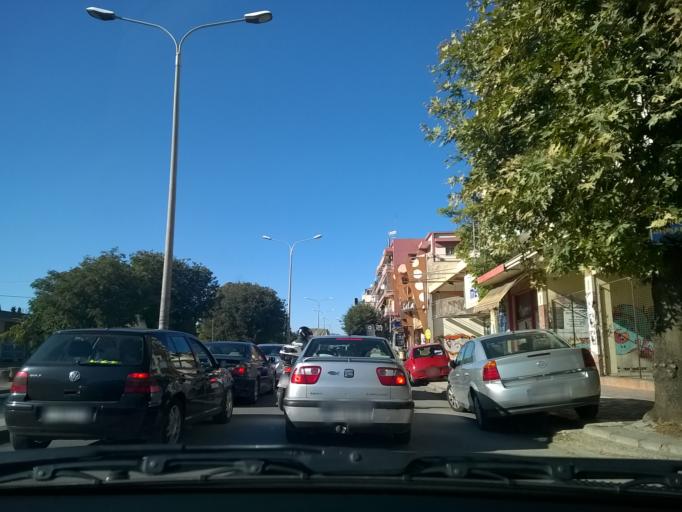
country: GR
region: Central Macedonia
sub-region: Nomos Thessalonikis
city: Ampelokipoi
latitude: 40.6527
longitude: 22.9353
